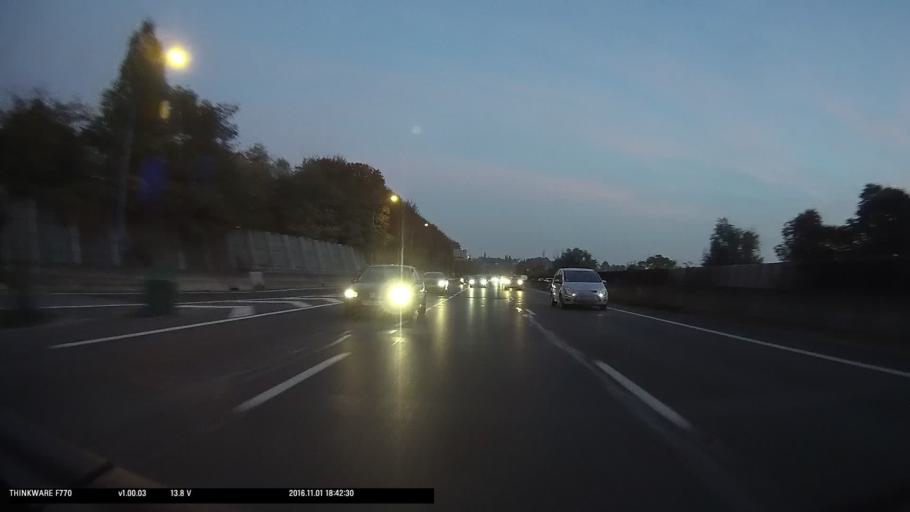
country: FR
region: Ile-de-France
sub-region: Departement de l'Essonne
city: Longjumeau
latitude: 48.6982
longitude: 2.3141
